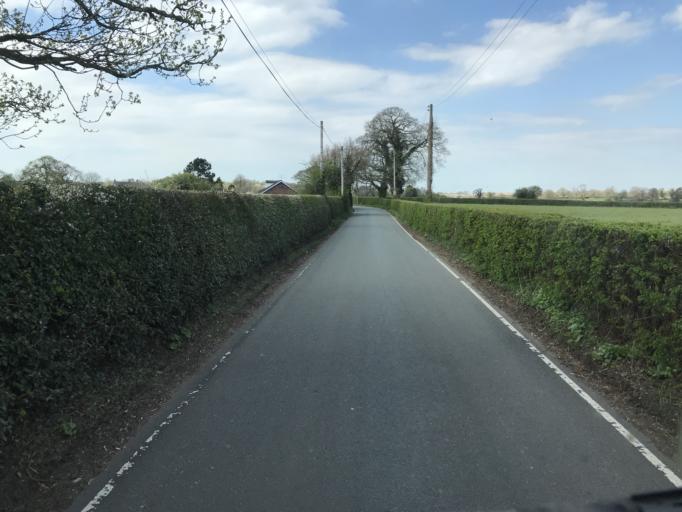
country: GB
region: England
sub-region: Cheshire West and Chester
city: Tarvin
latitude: 53.2105
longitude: -2.7695
